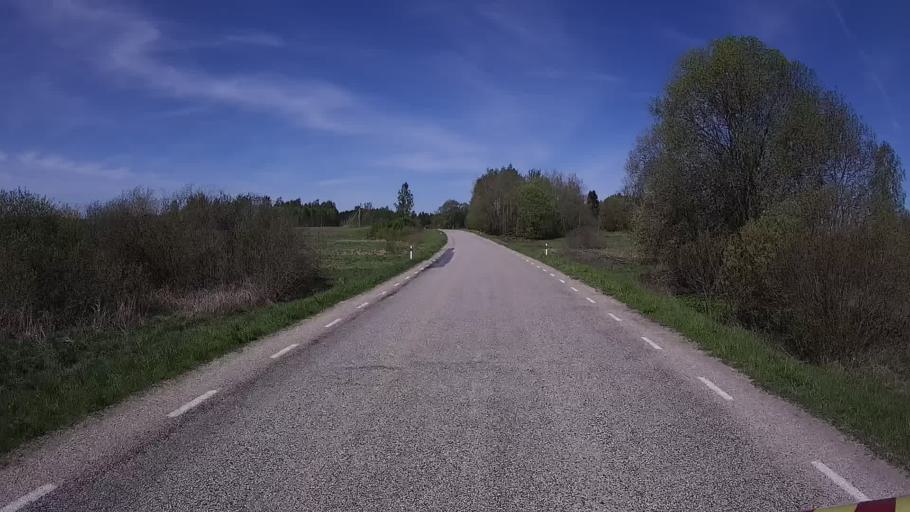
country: EE
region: Polvamaa
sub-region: Raepina vald
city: Rapina
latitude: 57.9677
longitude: 27.5277
